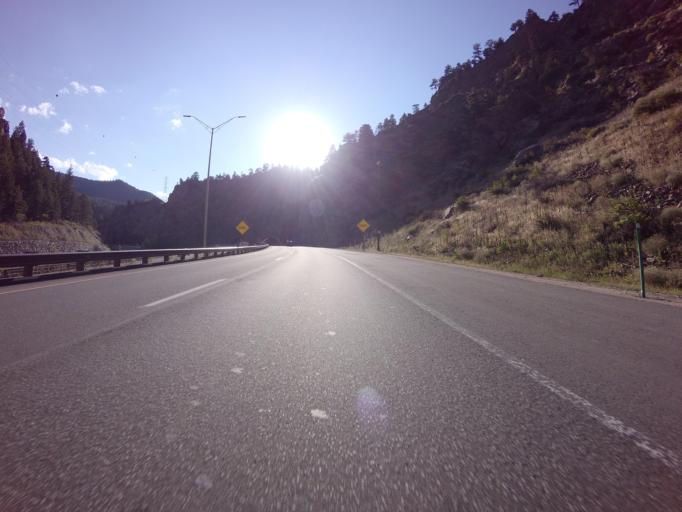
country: US
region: Colorado
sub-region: Clear Creek County
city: Idaho Springs
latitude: 39.7454
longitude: -105.4706
